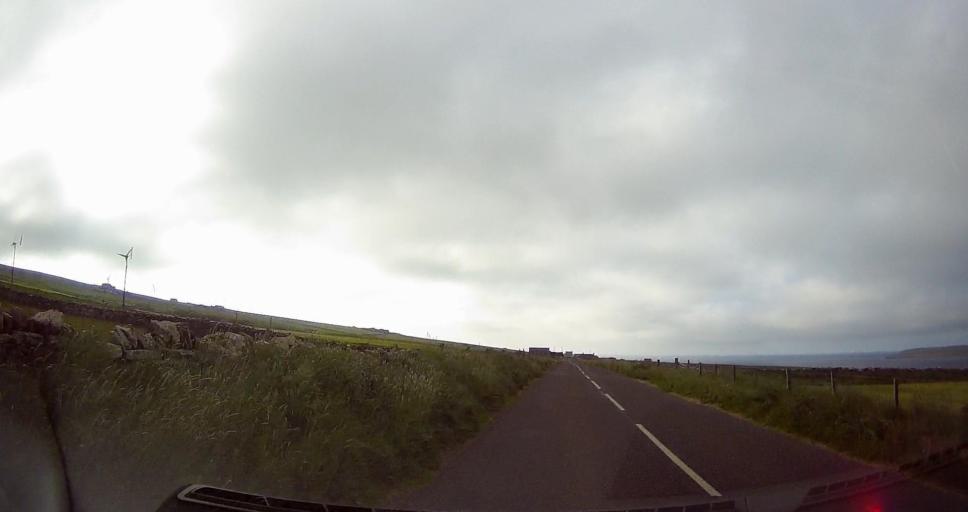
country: GB
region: Scotland
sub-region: Orkney Islands
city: Orkney
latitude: 59.1195
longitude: -3.1210
